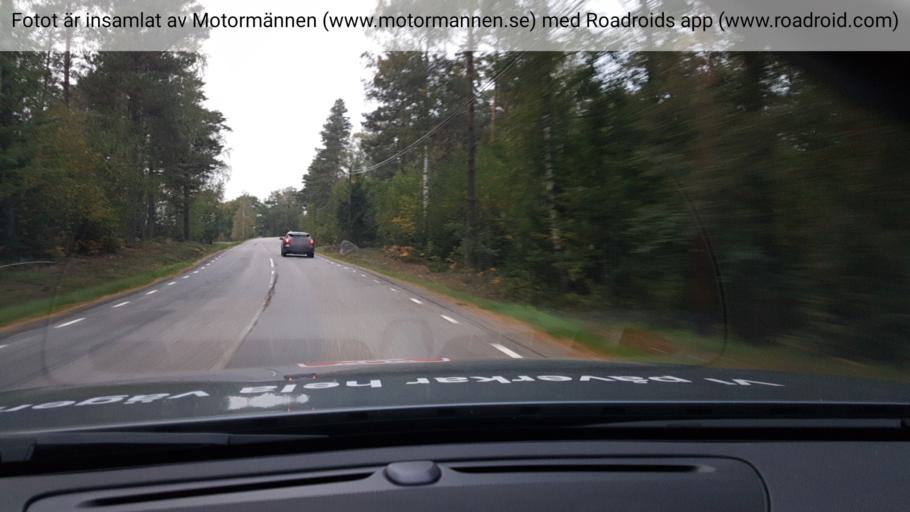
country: SE
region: Stockholm
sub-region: Haninge Kommun
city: Haninge
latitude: 59.0917
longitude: 18.1806
